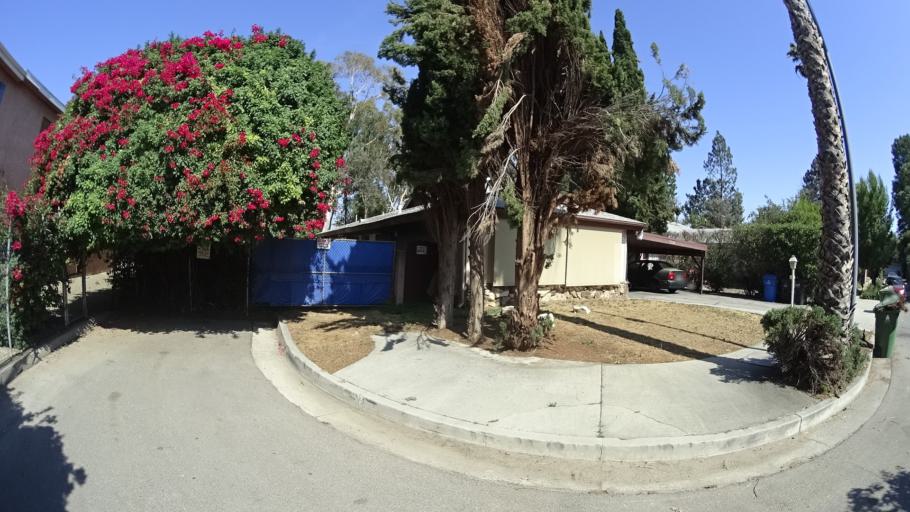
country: US
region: California
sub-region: Los Angeles County
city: Van Nuys
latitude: 34.2002
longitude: -118.4290
